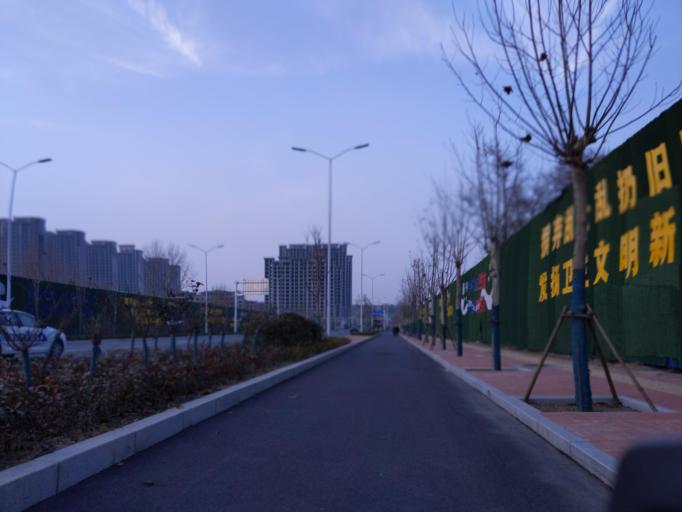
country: CN
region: Henan Sheng
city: Puyang
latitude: 35.8110
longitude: 115.0112
